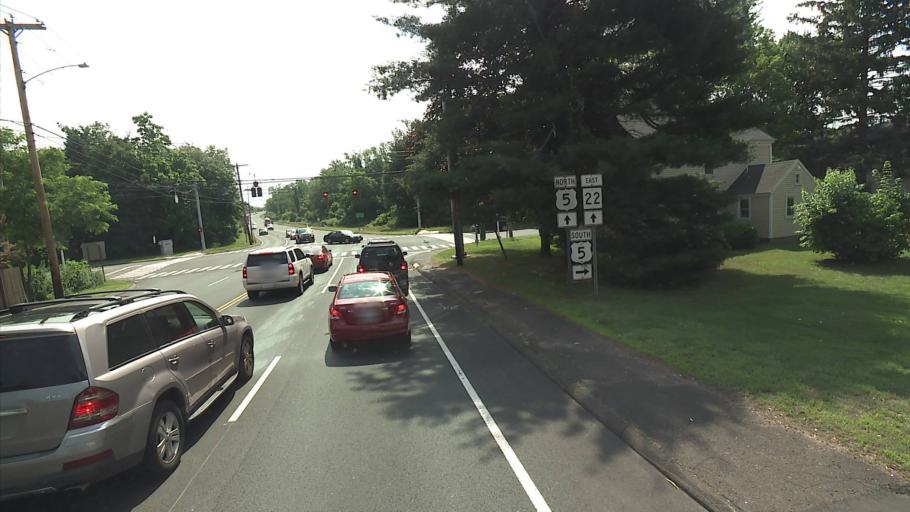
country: US
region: Connecticut
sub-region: New Haven County
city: North Haven
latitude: 41.3921
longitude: -72.8724
